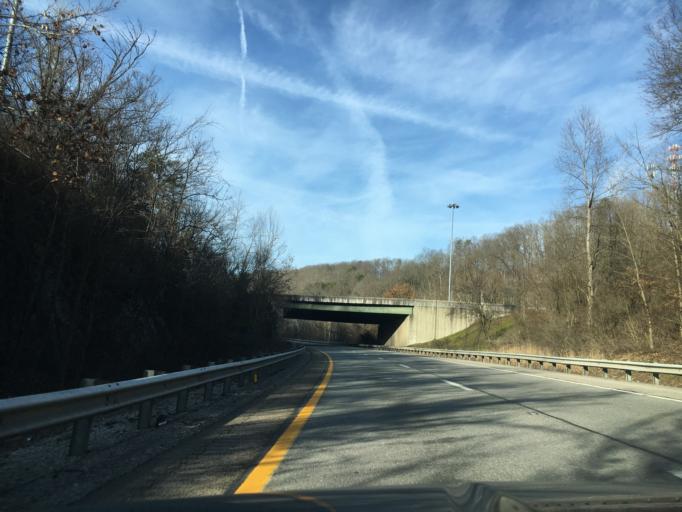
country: US
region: West Virginia
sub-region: Kanawha County
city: Charleston
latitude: 38.3760
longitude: -81.6058
